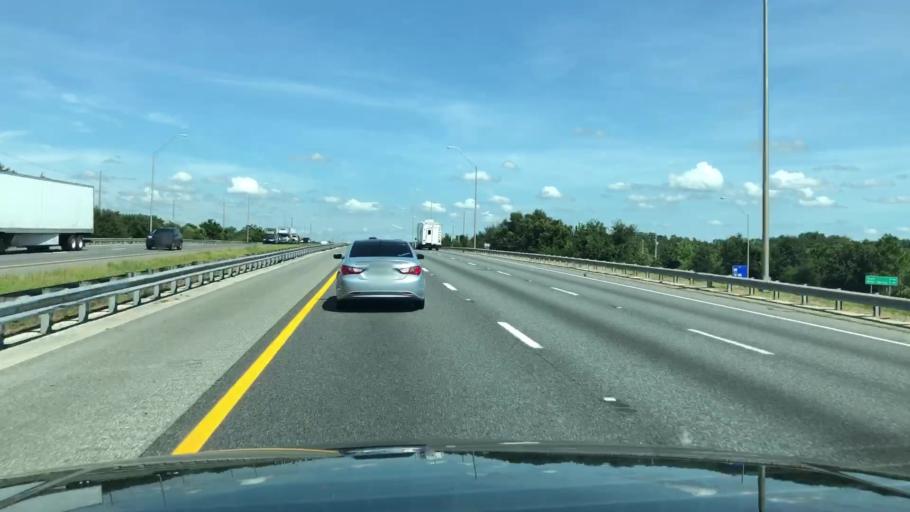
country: US
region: Florida
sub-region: Marion County
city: Ocala
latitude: 29.1843
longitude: -82.1845
